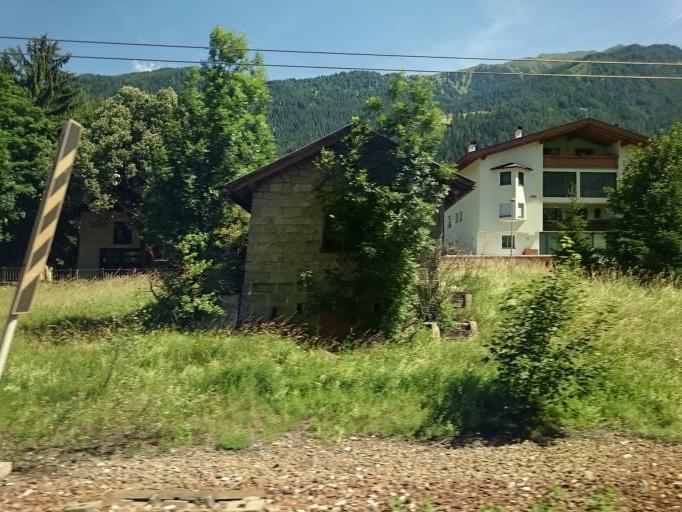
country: IT
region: Trentino-Alto Adige
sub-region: Bolzano
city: Campo di Trens
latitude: 46.8700
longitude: 11.4865
